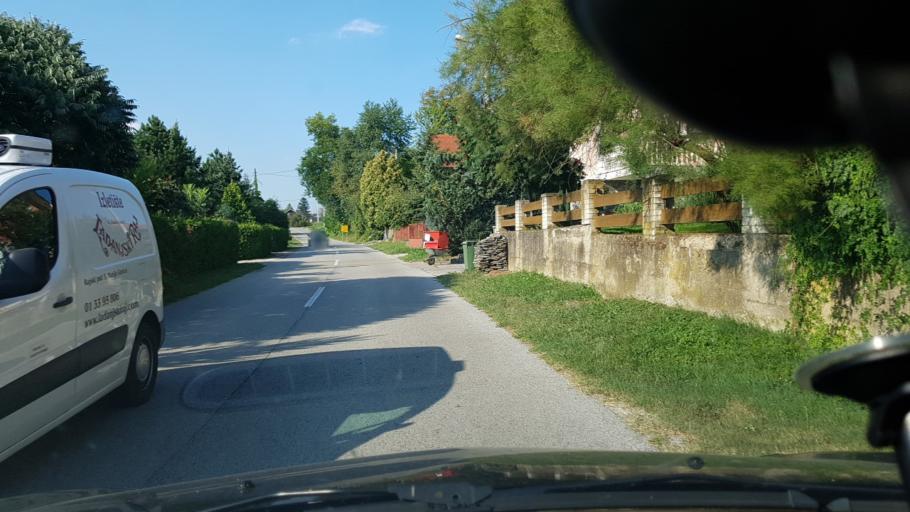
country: HR
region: Zagrebacka
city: Bregana
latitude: 45.9211
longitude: 15.7161
